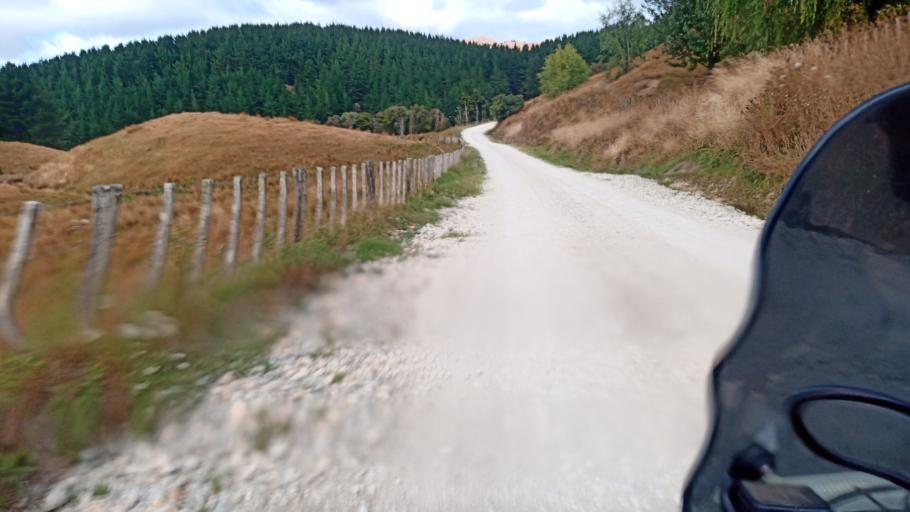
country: NZ
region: Hawke's Bay
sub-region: Wairoa District
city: Wairoa
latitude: -38.6052
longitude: 177.4928
